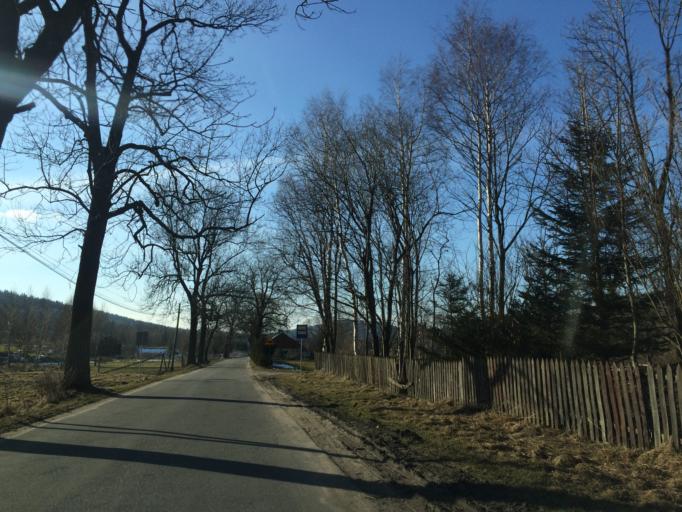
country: PL
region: Lower Silesian Voivodeship
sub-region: Powiat klodzki
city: Stronie Slaskie
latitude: 50.3033
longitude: 16.9479
